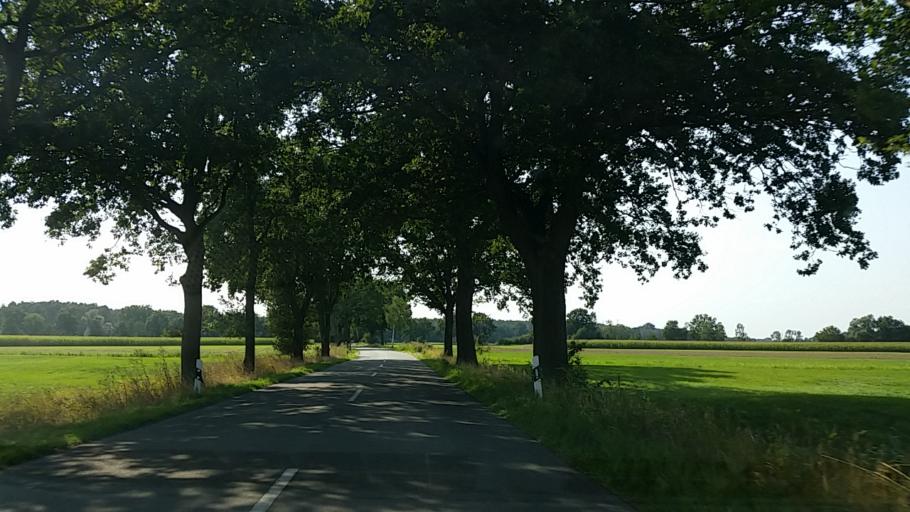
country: DE
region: Lower Saxony
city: Langendorf
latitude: 53.1154
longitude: 11.2360
